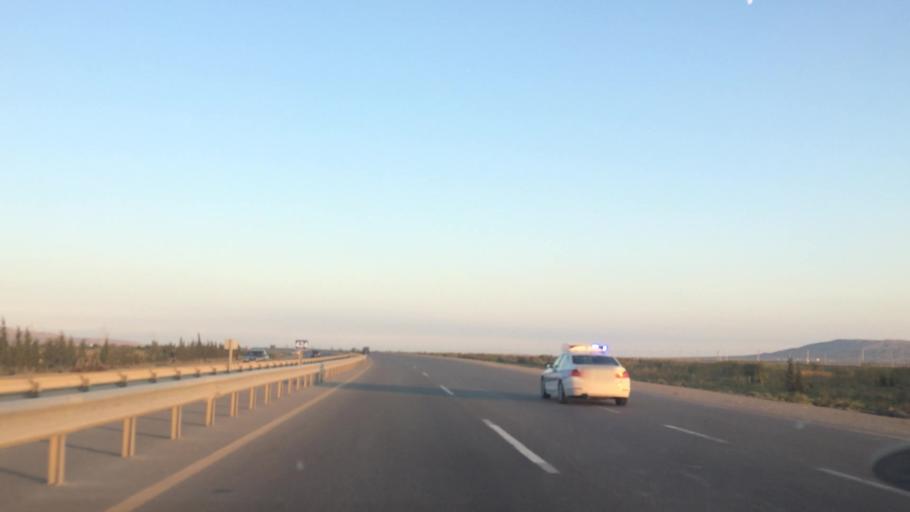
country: AZ
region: Baki
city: Qobustan
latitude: 39.9843
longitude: 49.2127
